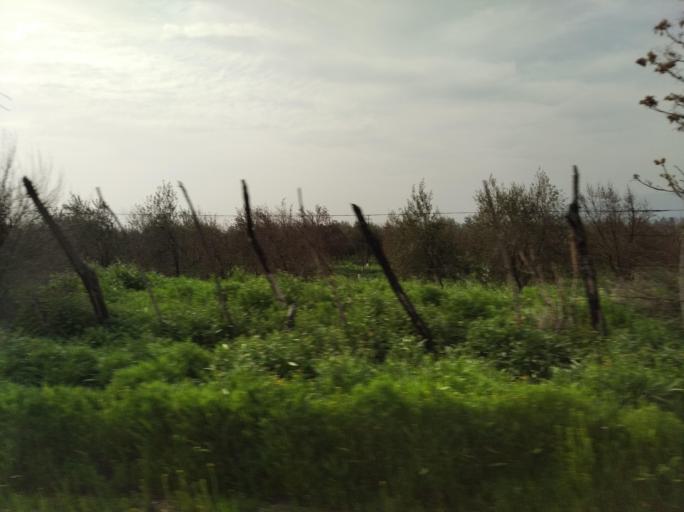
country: CL
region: Santiago Metropolitan
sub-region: Provincia de Chacabuco
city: Lampa
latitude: -33.1647
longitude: -70.8940
